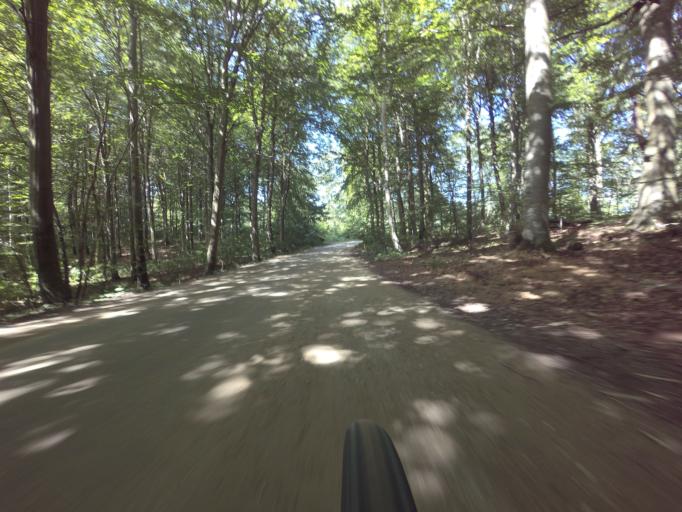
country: DK
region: Zealand
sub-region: Vordingborg Kommune
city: Stege
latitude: 54.9730
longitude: 12.5332
